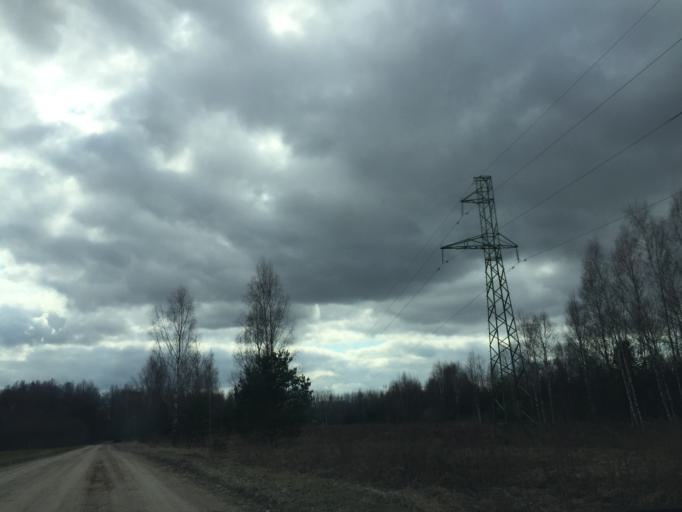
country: LV
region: Vecumnieki
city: Vecumnieki
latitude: 56.5820
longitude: 24.6067
